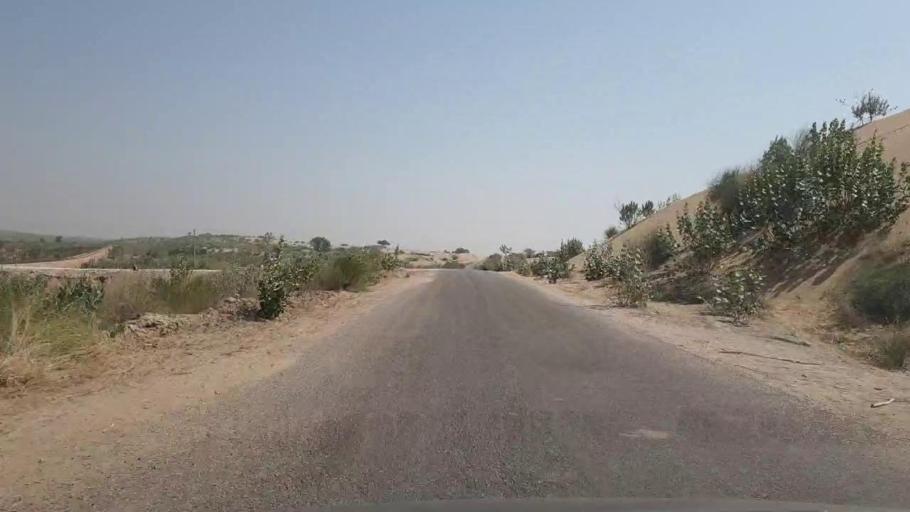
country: PK
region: Sindh
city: Chor
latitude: 25.6693
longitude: 70.1571
